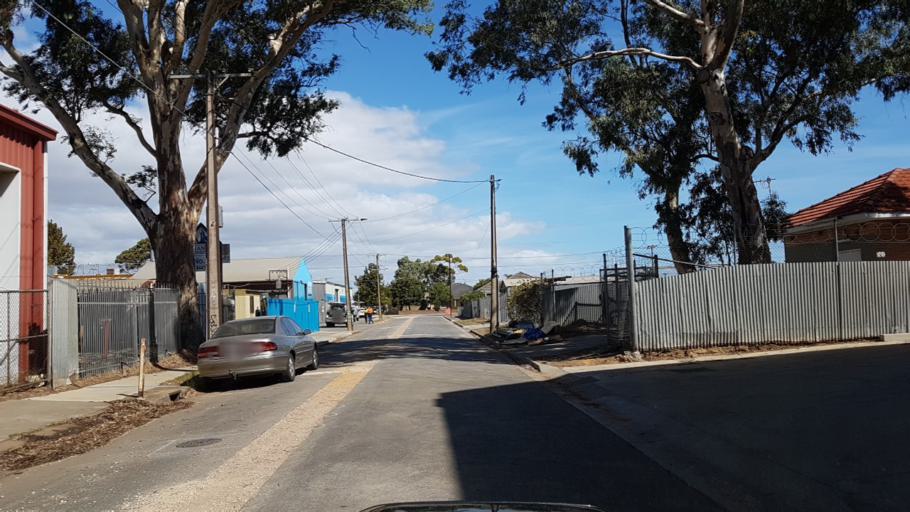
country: AU
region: South Australia
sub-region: Charles Sturt
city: Woodville North
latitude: -34.8533
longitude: 138.5424
